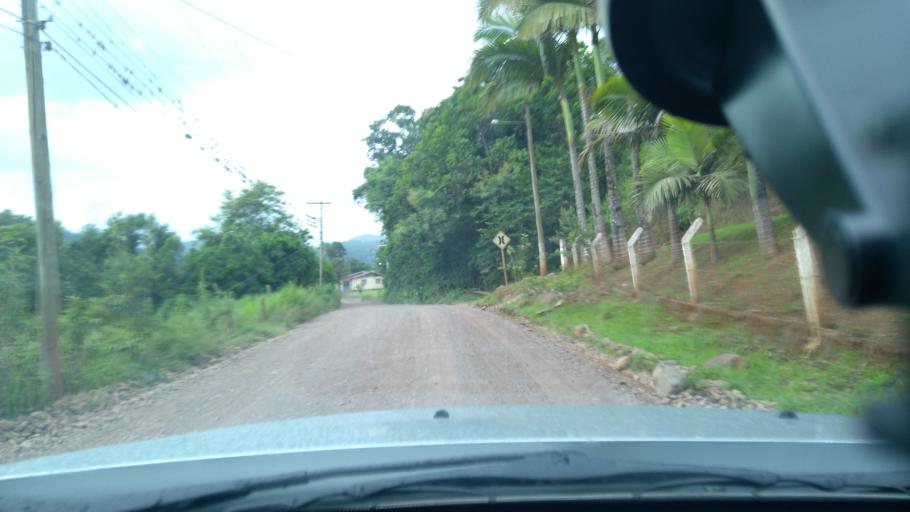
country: BR
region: Rio Grande do Sul
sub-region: Torres
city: Torres
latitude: -29.2035
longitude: -49.9713
